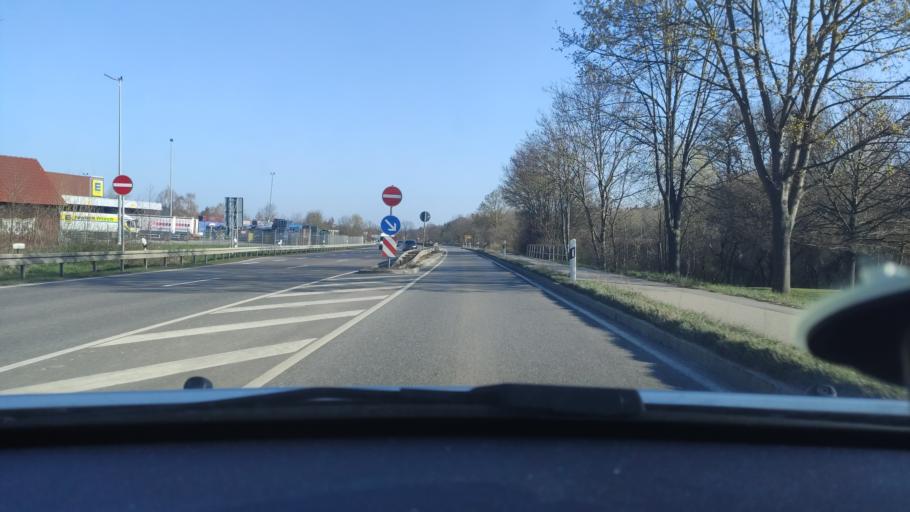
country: DE
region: Baden-Wuerttemberg
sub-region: Tuebingen Region
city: Balingen
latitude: 48.2539
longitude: 8.8557
